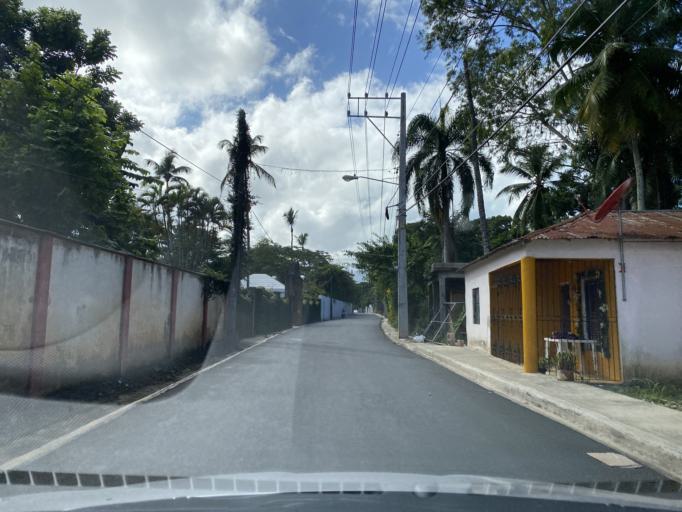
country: DO
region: Samana
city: Las Terrenas
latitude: 19.3102
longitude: -69.5491
